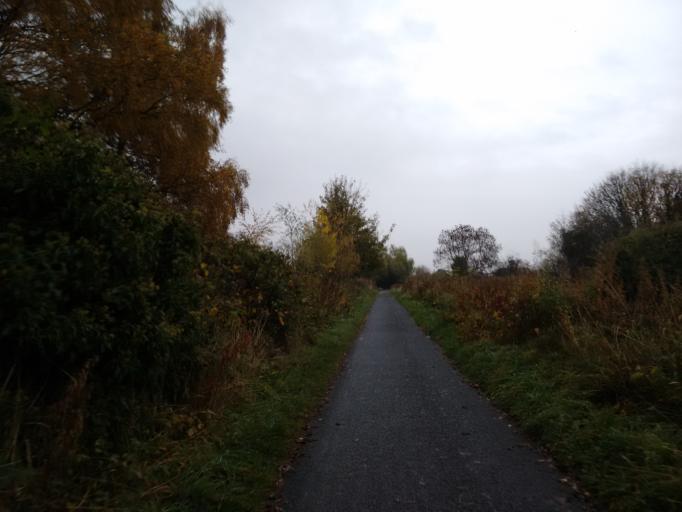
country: GB
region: Scotland
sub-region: Edinburgh
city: Colinton
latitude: 55.9224
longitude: -3.2519
